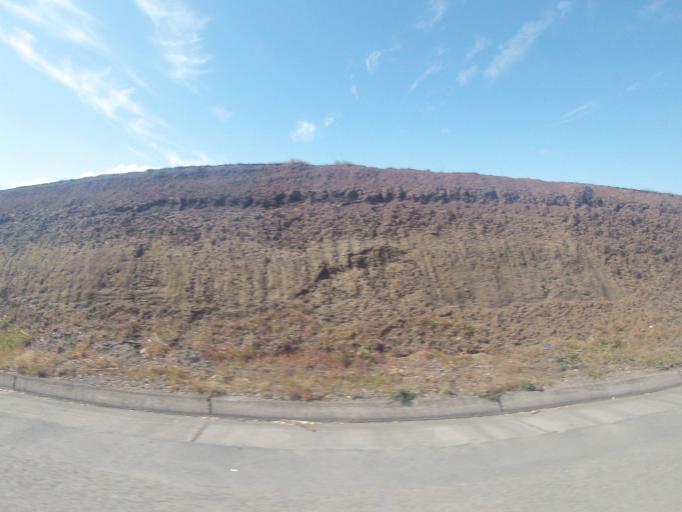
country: CL
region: Biobio
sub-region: Provincia de Biobio
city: Los Angeles
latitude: -37.4538
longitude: -72.4090
